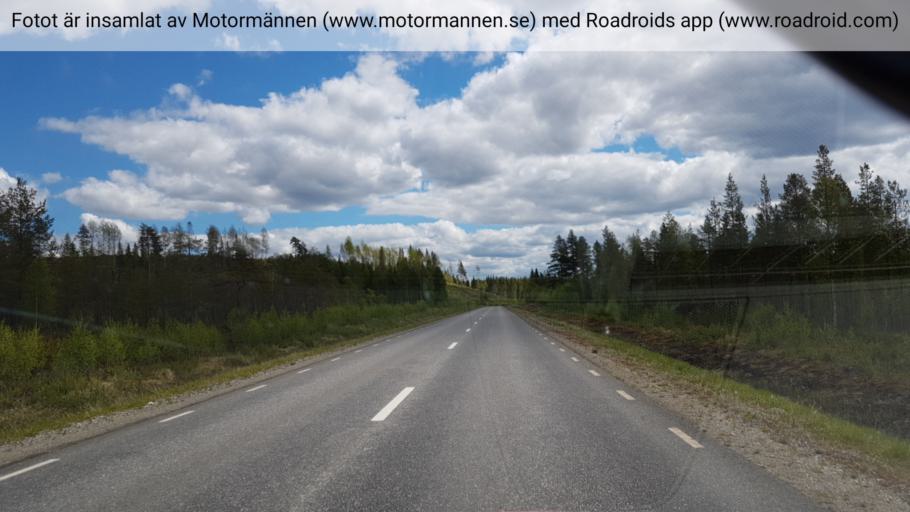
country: SE
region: Vaesterbotten
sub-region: Norsjo Kommun
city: Norsjoe
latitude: 64.8885
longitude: 19.6353
